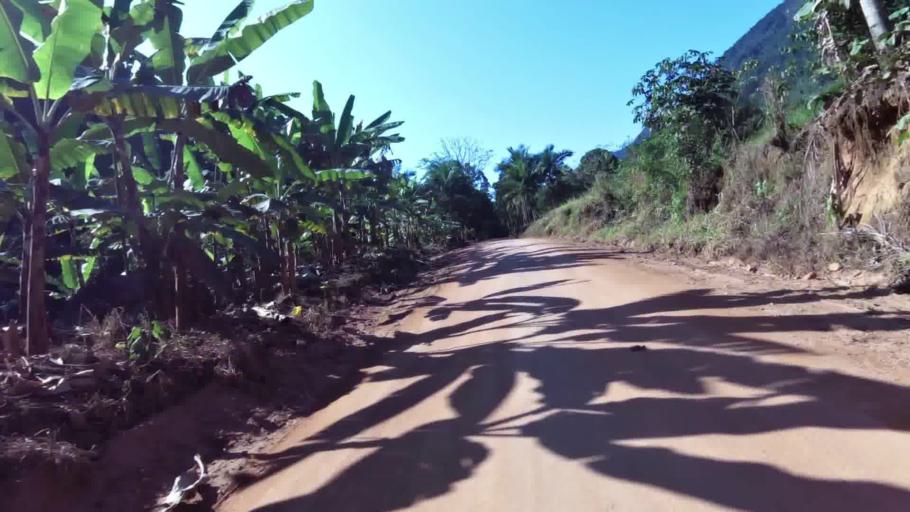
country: BR
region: Espirito Santo
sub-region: Alfredo Chaves
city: Alfredo Chaves
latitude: -20.5521
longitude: -40.7268
